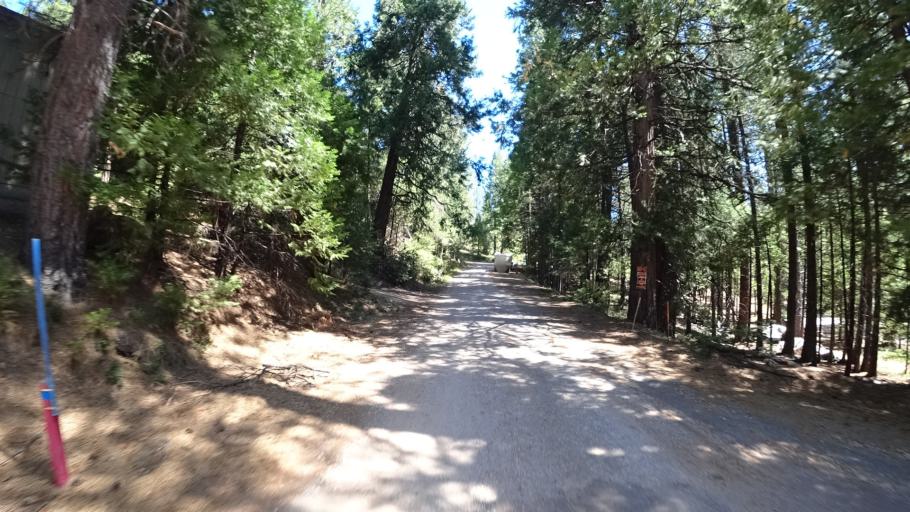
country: US
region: California
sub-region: Amador County
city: Pioneer
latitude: 38.4448
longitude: -120.4297
